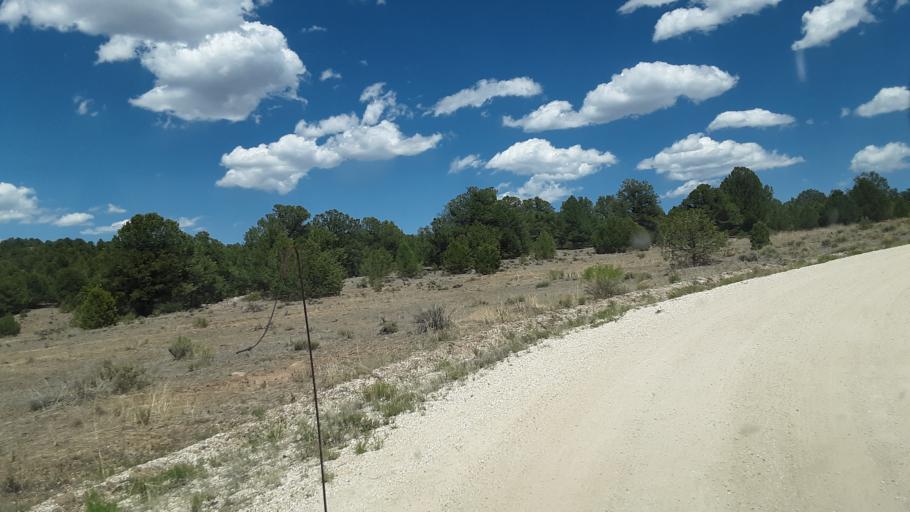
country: US
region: Colorado
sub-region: Custer County
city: Westcliffe
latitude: 38.3287
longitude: -105.6321
